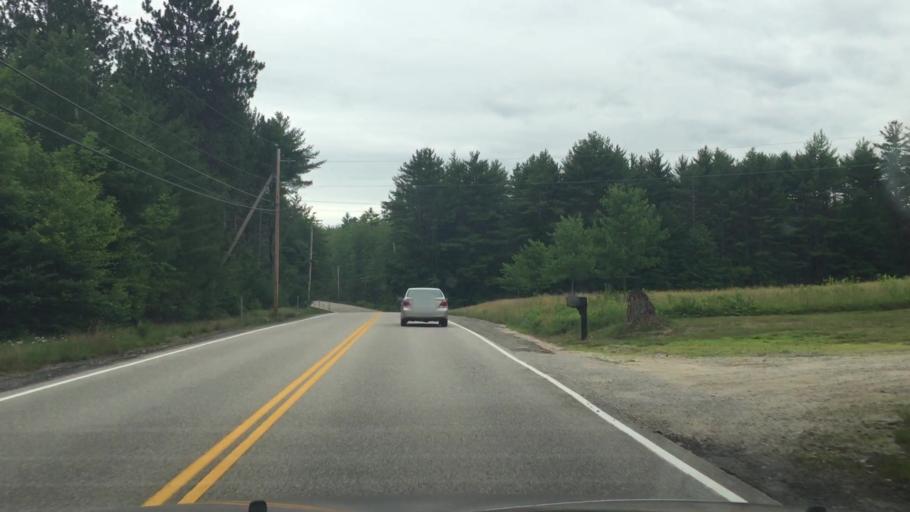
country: US
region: New Hampshire
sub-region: Carroll County
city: Conway
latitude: 43.9668
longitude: -71.1095
